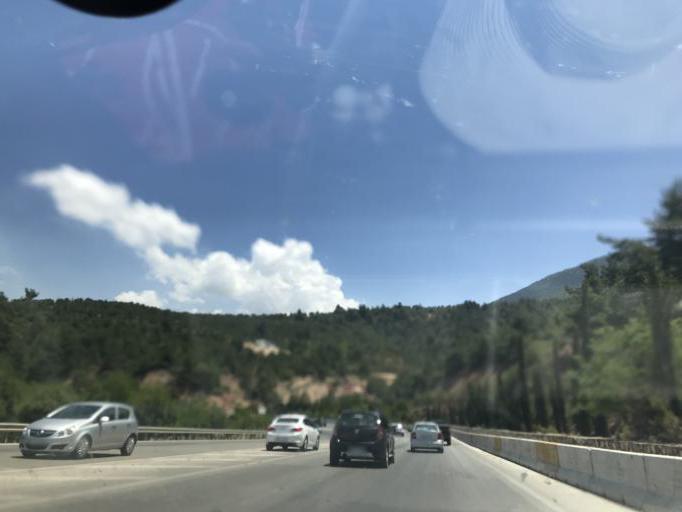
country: TR
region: Denizli
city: Denizli
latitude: 37.7299
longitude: 29.1696
